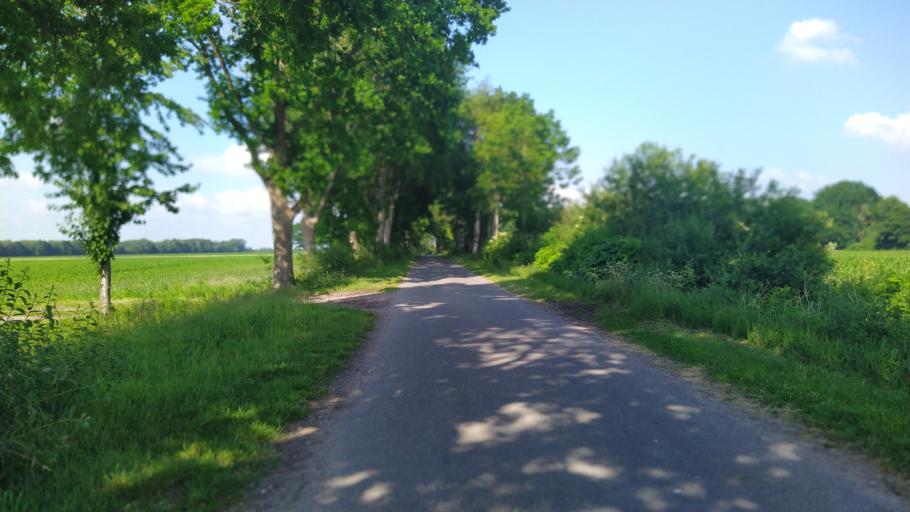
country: DE
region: Lower Saxony
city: Wohnste
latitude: 53.3918
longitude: 9.5518
